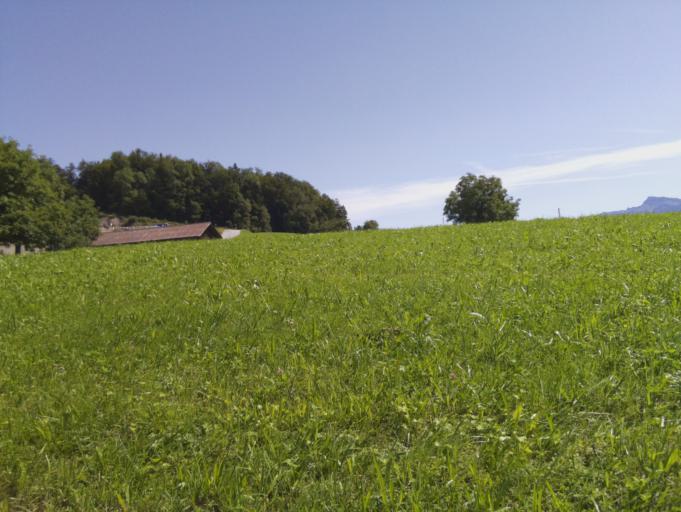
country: CH
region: Schwyz
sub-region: Bezirk March
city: Schubelbach
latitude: 47.1949
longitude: 8.9103
